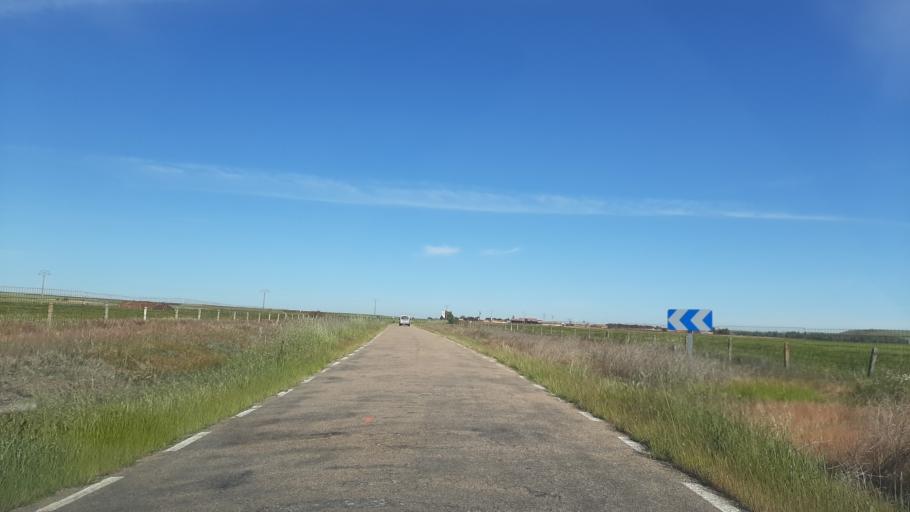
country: ES
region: Castille and Leon
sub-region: Provincia de Salamanca
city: Gajates
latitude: 40.8010
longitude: -5.3761
